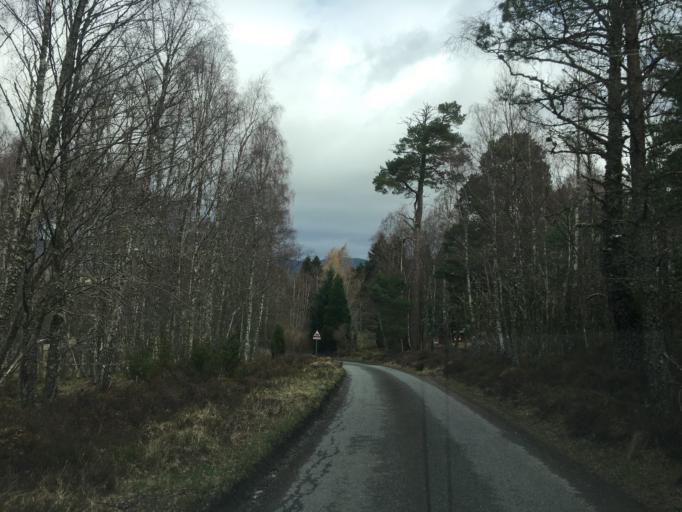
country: GB
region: Scotland
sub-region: Highland
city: Aviemore
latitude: 57.1079
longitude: -3.9204
